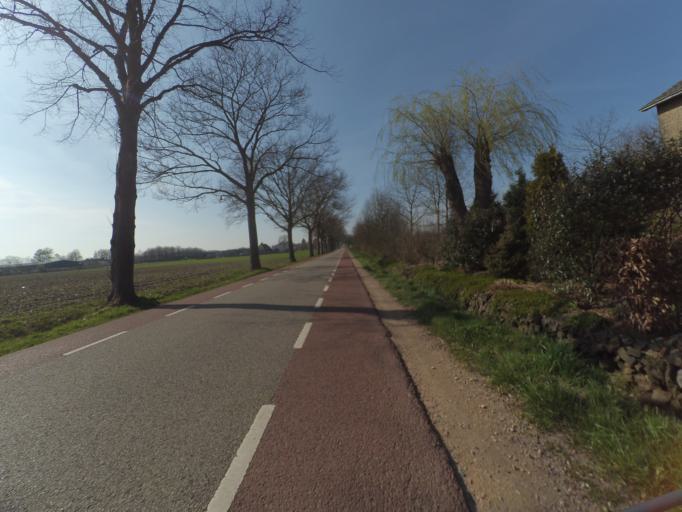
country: NL
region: Gelderland
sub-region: Gemeente Groesbeek
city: De Horst
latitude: 51.7800
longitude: 5.9597
